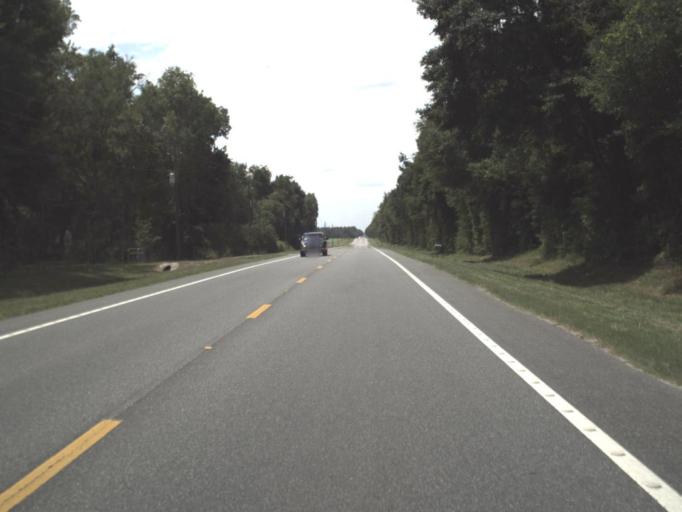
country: US
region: Florida
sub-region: Suwannee County
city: Wellborn
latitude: 30.0757
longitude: -82.9446
